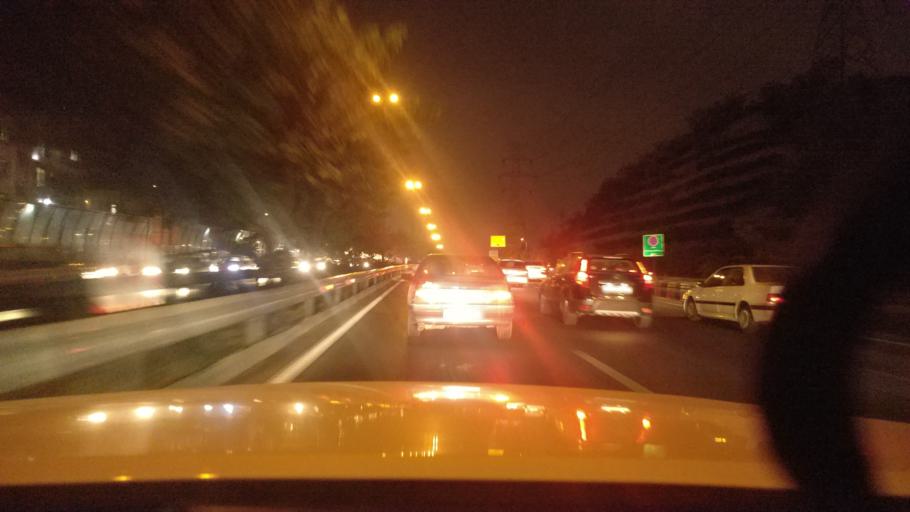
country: IR
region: Tehran
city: Tehran
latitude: 35.7410
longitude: 51.3808
